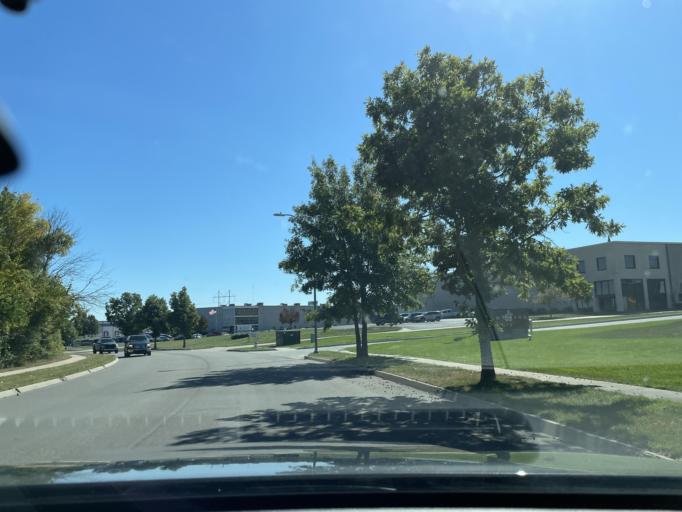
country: US
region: Missouri
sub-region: Buchanan County
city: Saint Joseph
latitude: 39.7520
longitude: -94.7647
